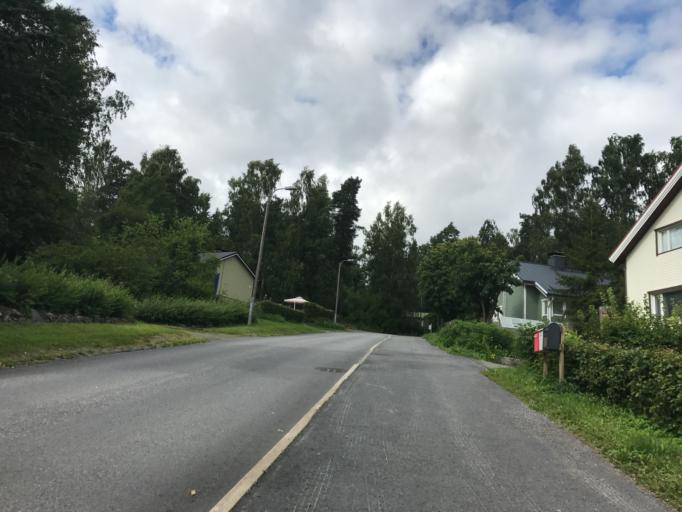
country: FI
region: Pirkanmaa
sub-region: Etelae-Pirkanmaa
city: Valkeakoski
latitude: 61.2578
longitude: 24.0447
